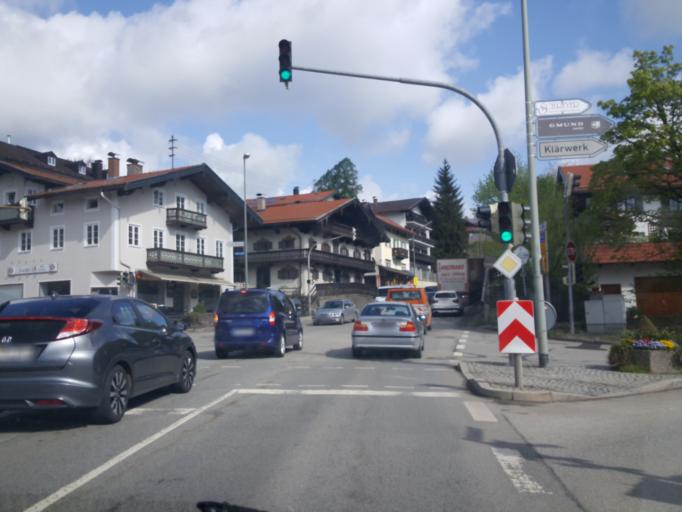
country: DE
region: Bavaria
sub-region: Upper Bavaria
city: Gmund am Tegernsee
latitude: 47.7504
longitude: 11.7387
